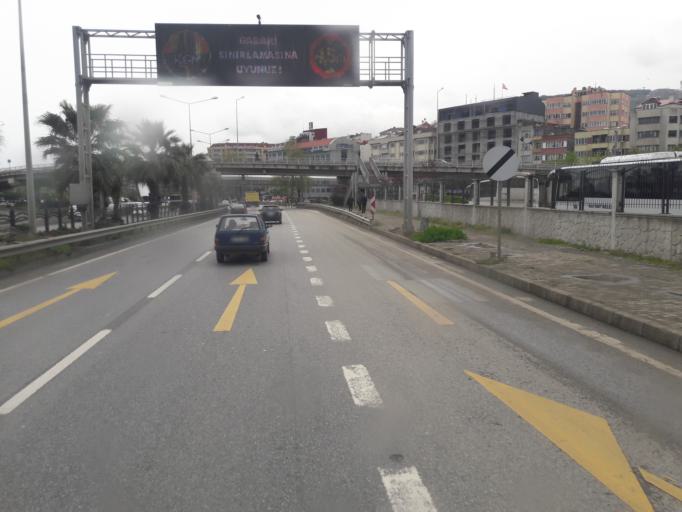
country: TR
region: Trabzon
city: Trabzon
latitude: 41.0097
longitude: 39.7259
